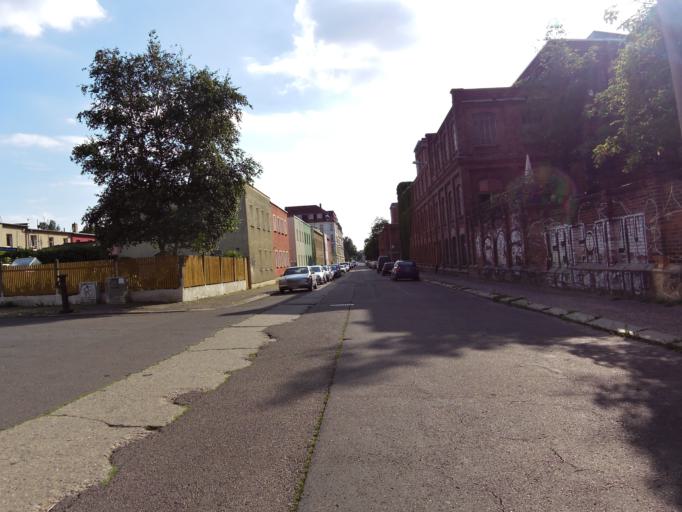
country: DE
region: Saxony
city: Leipzig
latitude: 51.3268
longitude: 12.3208
